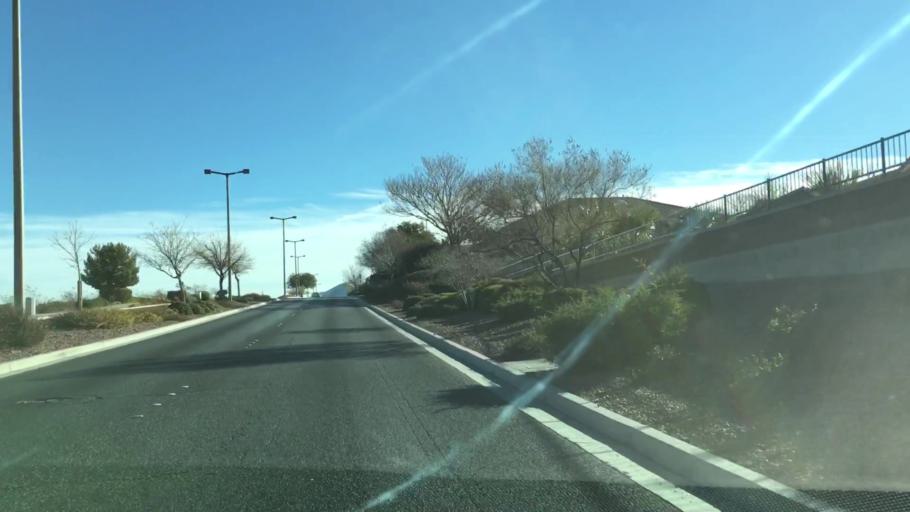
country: US
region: Nevada
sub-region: Clark County
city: Whitney
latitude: 35.9693
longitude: -115.1118
